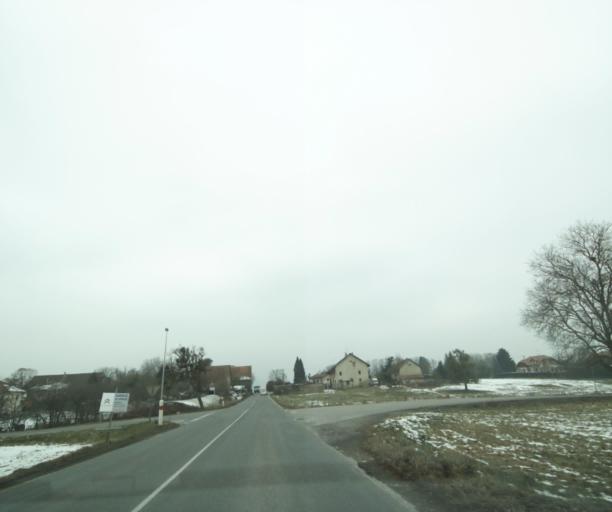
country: FR
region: Rhone-Alpes
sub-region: Departement de la Haute-Savoie
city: Reignier-Esery
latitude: 46.1371
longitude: 6.2892
